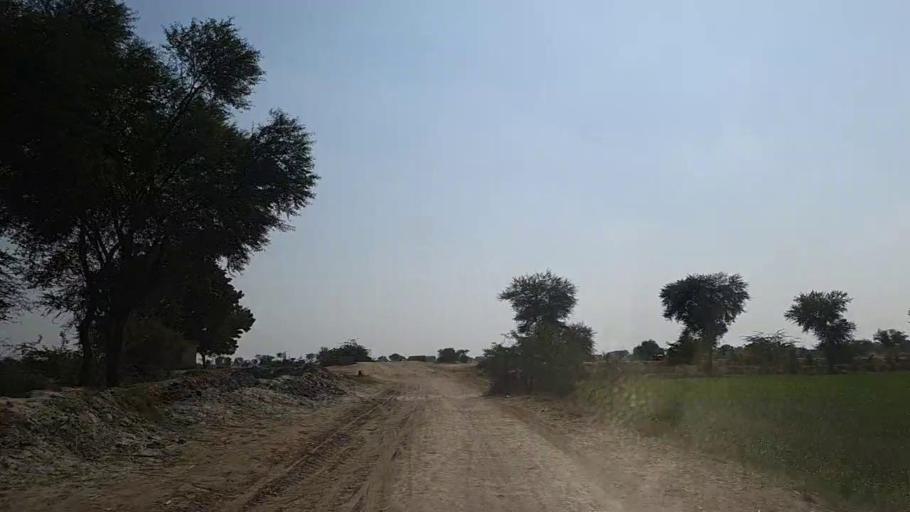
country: PK
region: Sindh
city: Daur
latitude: 26.4780
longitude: 68.2498
